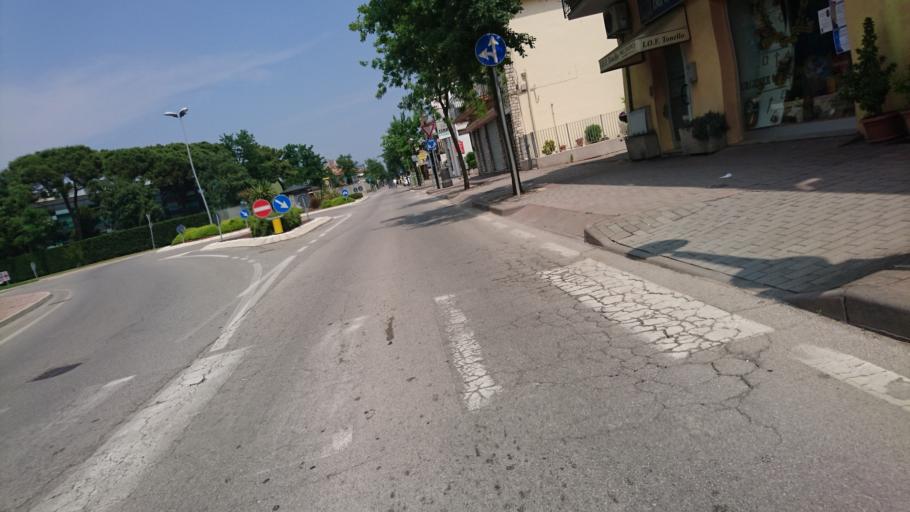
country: IT
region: Veneto
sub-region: Provincia di Venezia
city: Chioggia
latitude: 45.1980
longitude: 12.2848
